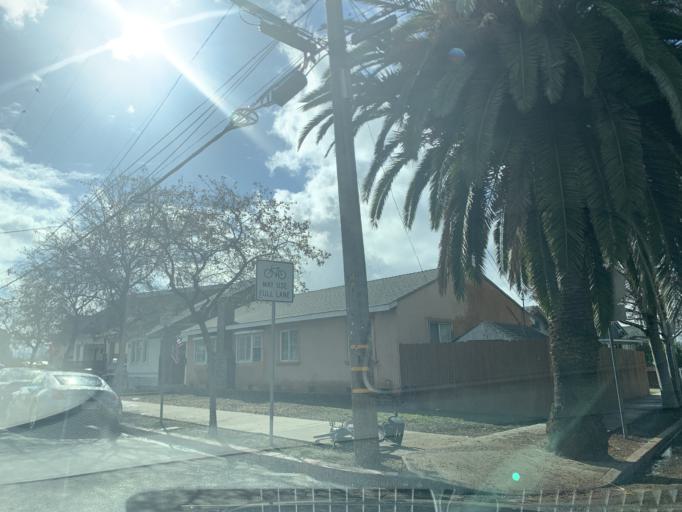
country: US
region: California
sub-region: Santa Clara County
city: San Jose
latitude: 37.3154
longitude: -121.8847
